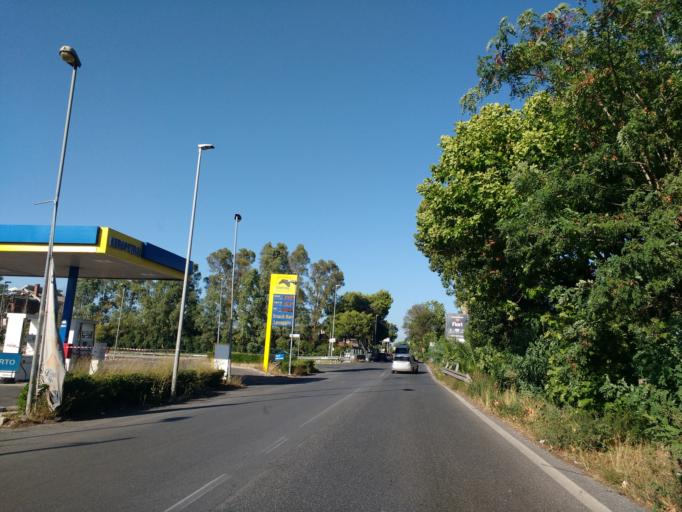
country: IT
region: Latium
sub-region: Citta metropolitana di Roma Capitale
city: Acilia-Castel Fusano-Ostia Antica
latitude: 41.7640
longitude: 12.3104
